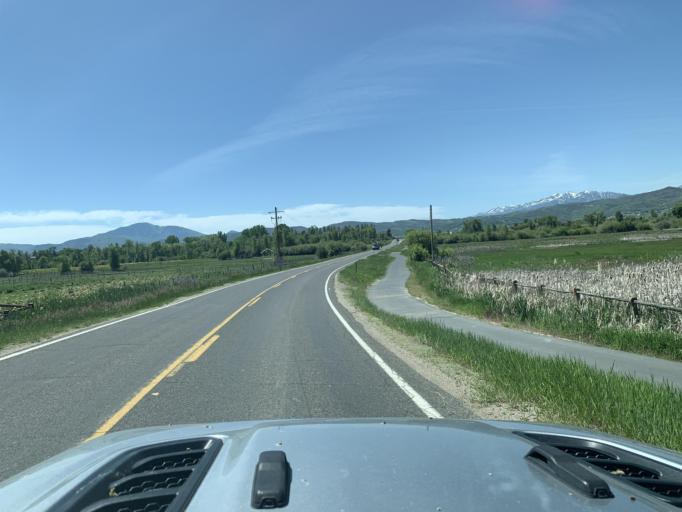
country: US
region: Utah
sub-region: Weber County
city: Wolf Creek
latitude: 41.2914
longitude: -111.7773
